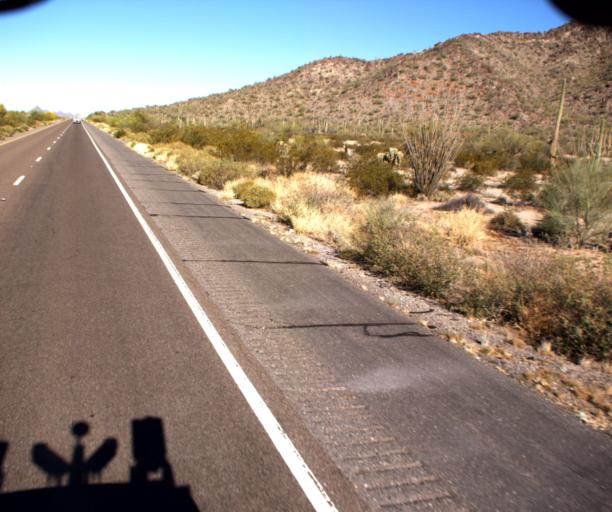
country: US
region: Arizona
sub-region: Maricopa County
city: Gila Bend
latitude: 32.8618
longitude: -112.3998
